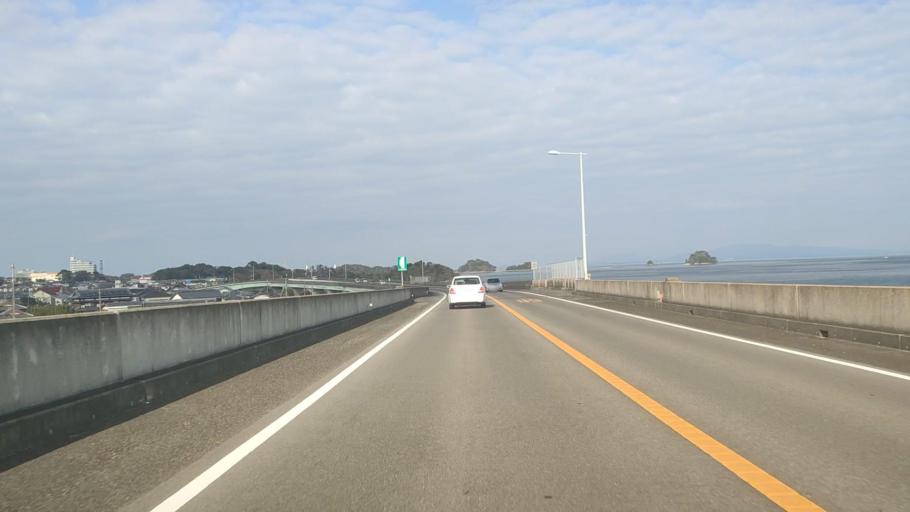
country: JP
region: Nagasaki
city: Shimabara
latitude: 32.7500
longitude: 130.3738
